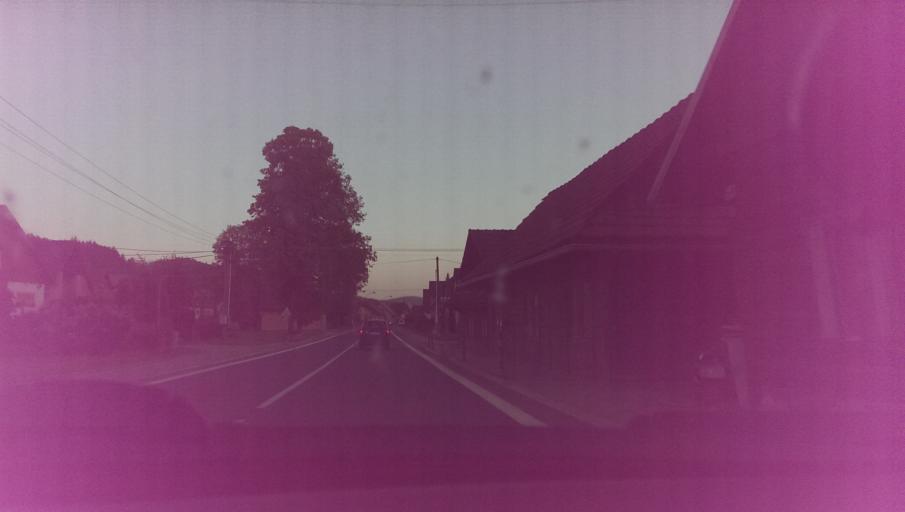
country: CZ
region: Zlin
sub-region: Okres Vsetin
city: Vsetin
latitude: 49.3077
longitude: 18.0030
